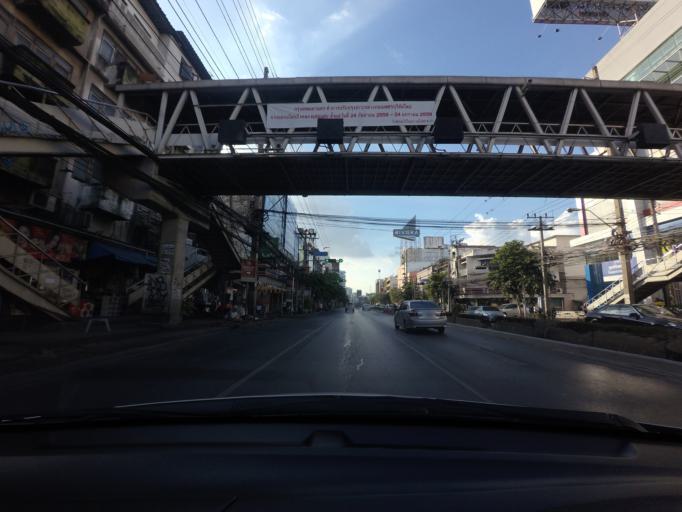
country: TH
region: Bangkok
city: Watthana
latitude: 13.7446
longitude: 100.5851
